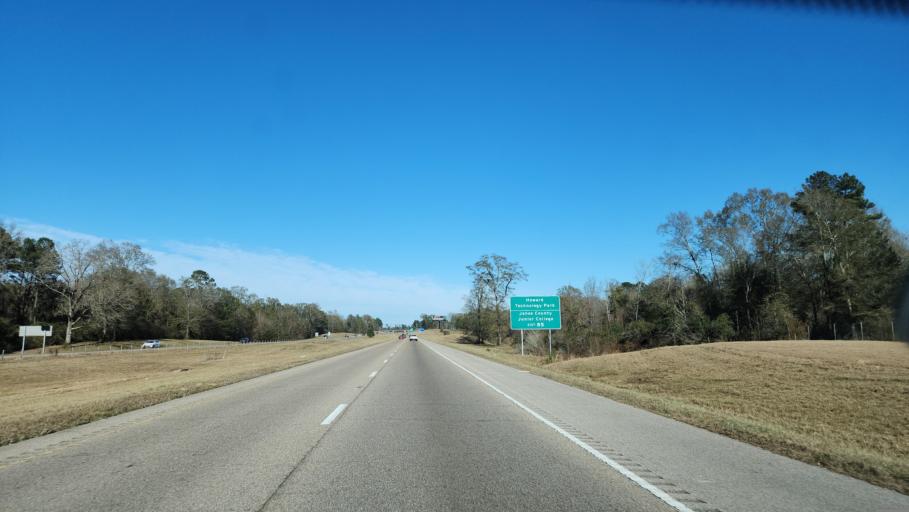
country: US
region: Mississippi
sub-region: Jones County
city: Ellisville
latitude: 31.5759
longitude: -89.2454
